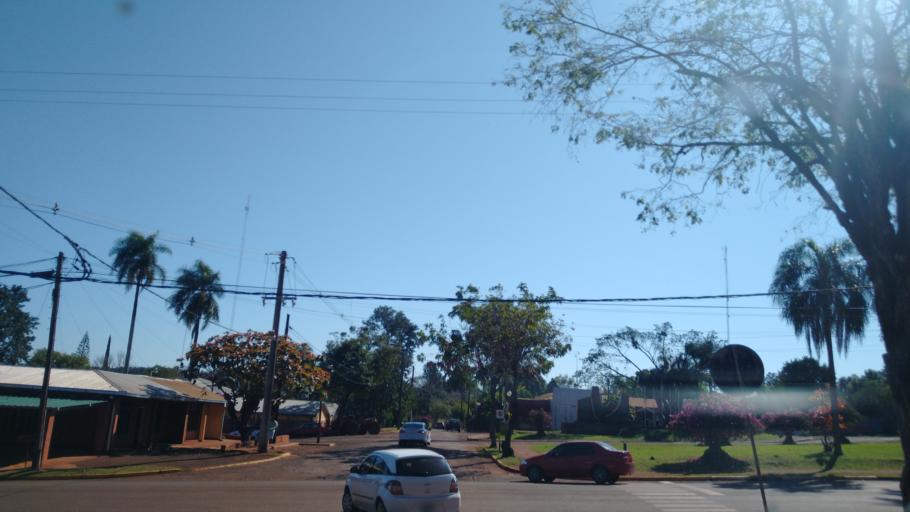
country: AR
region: Misiones
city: Puerto Libertad
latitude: -25.9723
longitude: -54.5609
